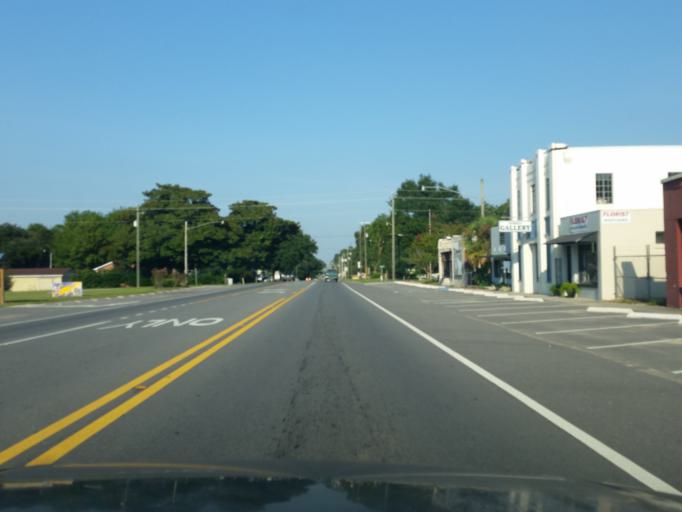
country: US
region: Alabama
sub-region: Baldwin County
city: Elberta
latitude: 30.4143
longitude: -87.5980
